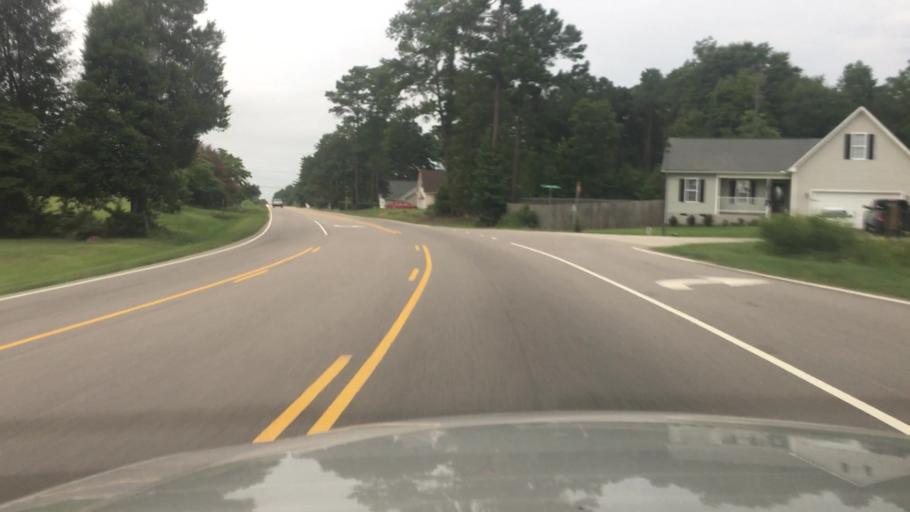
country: US
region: North Carolina
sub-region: Hoke County
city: Rockfish
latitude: 34.9678
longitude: -79.0528
